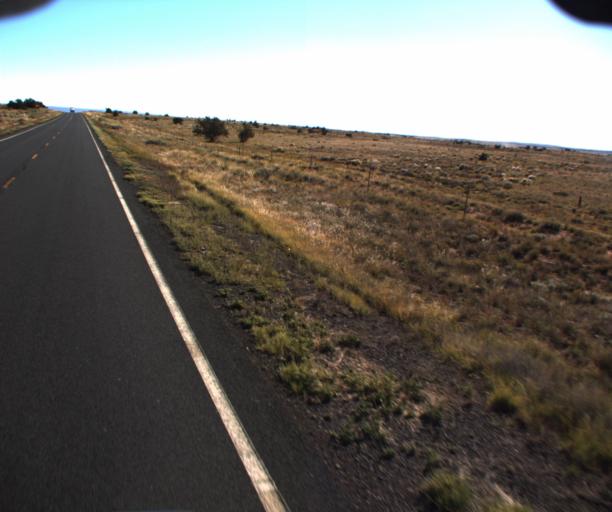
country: US
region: Arizona
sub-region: Apache County
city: Houck
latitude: 35.2431
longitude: -109.4391
